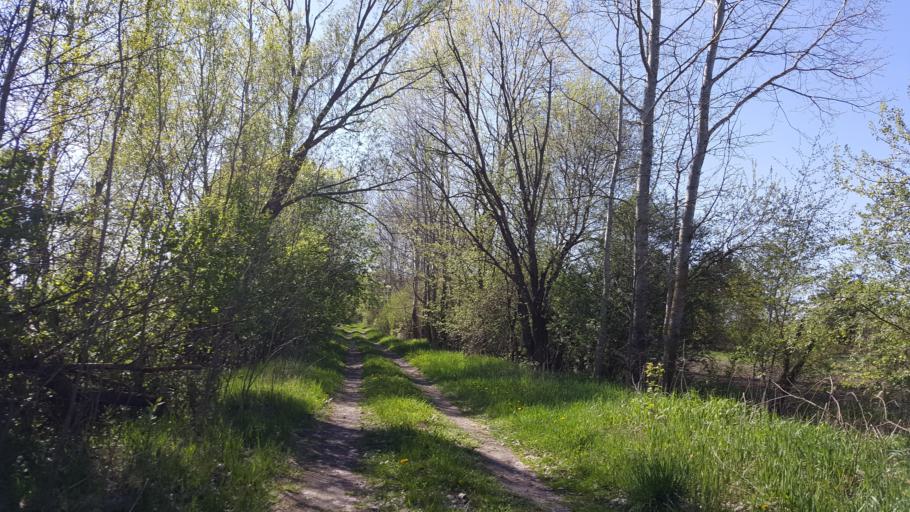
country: BY
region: Brest
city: Kamyanyets
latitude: 52.4336
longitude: 23.8805
